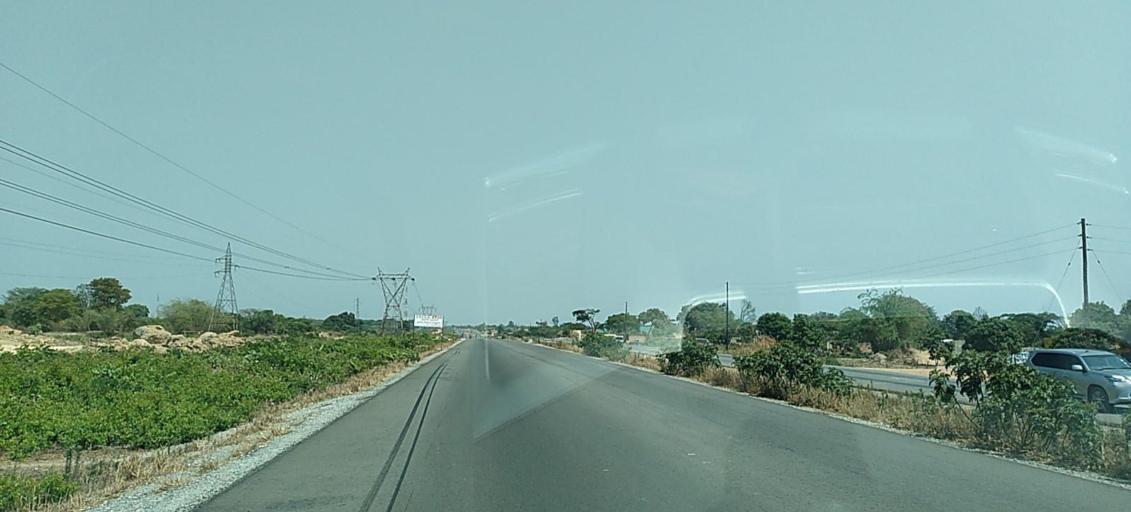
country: ZM
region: Copperbelt
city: Chambishi
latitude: -12.6018
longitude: 27.9665
